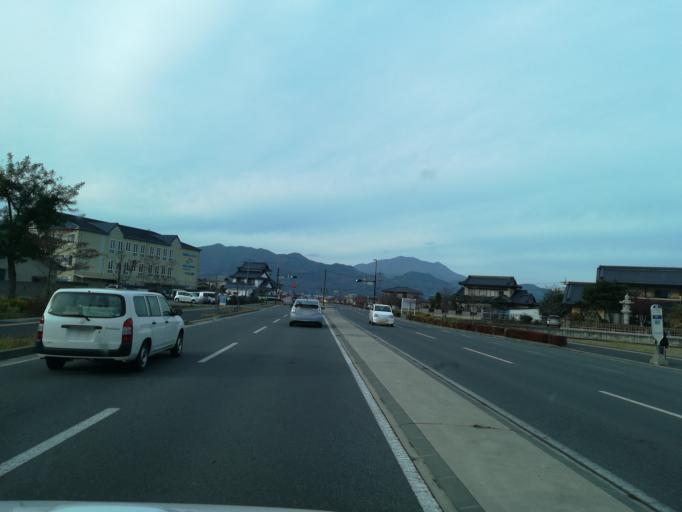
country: JP
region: Nagano
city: Nagano-shi
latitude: 36.5966
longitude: 138.1827
